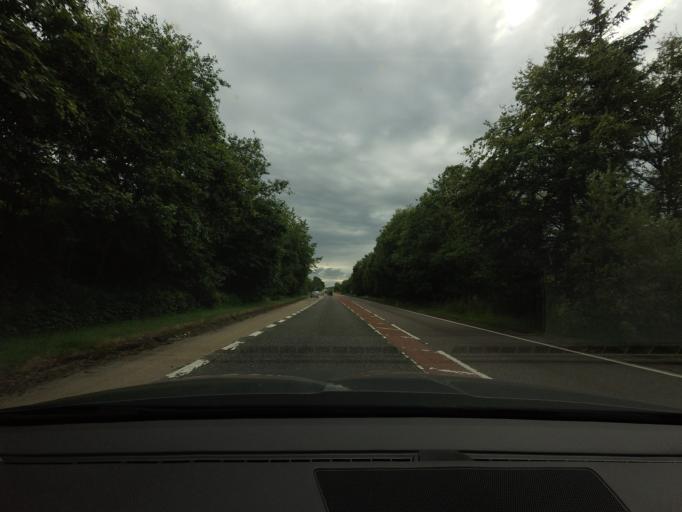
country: GB
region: Scotland
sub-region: Highland
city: Evanton
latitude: 57.6711
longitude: -4.3134
